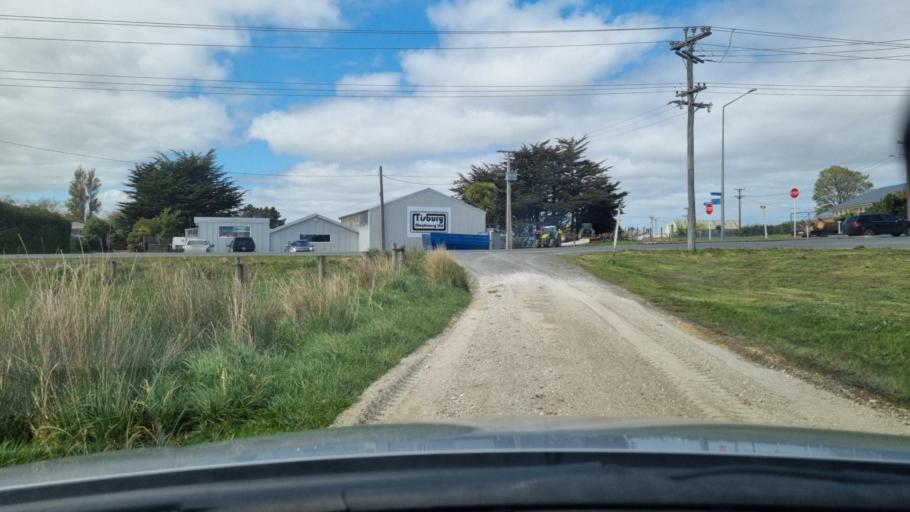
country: NZ
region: Southland
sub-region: Invercargill City
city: Invercargill
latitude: -46.4440
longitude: 168.3987
